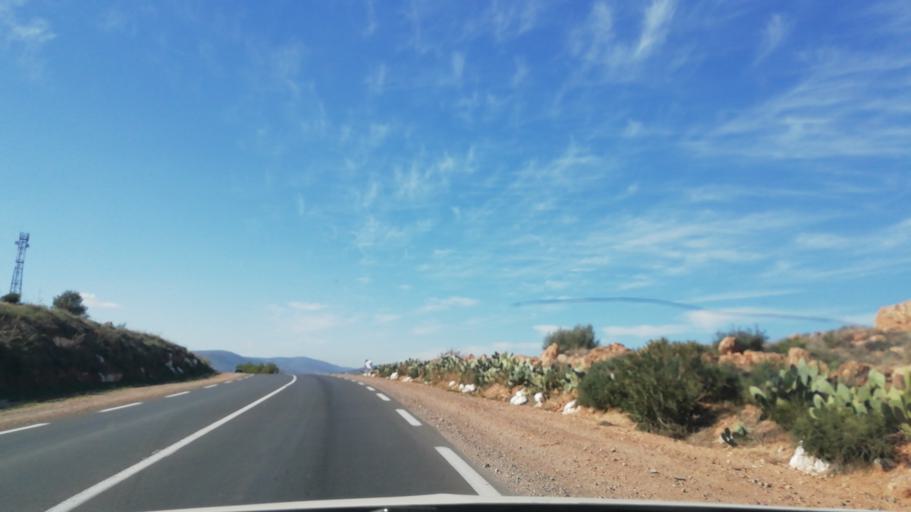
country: DZ
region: Tlemcen
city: Ouled Mimoun
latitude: 34.8771
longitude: -1.1156
